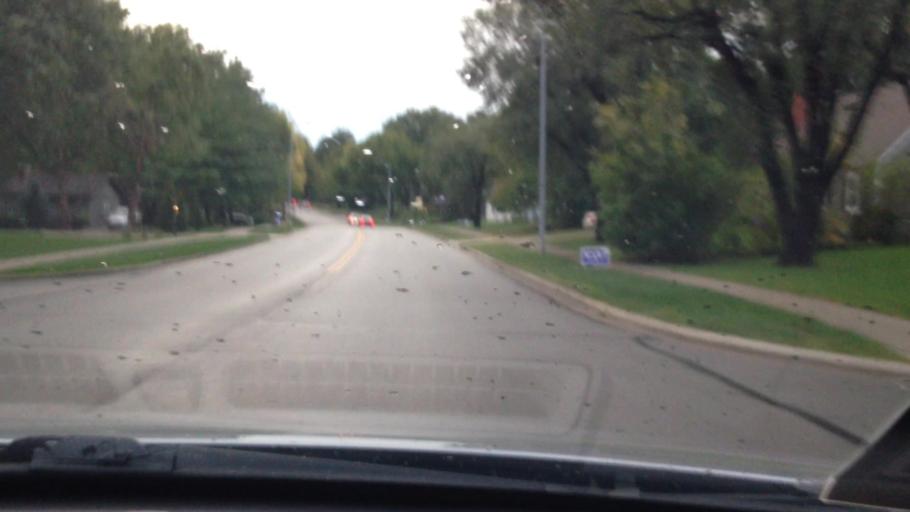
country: US
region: Kansas
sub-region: Johnson County
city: Prairie Village
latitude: 38.9842
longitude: -94.6192
